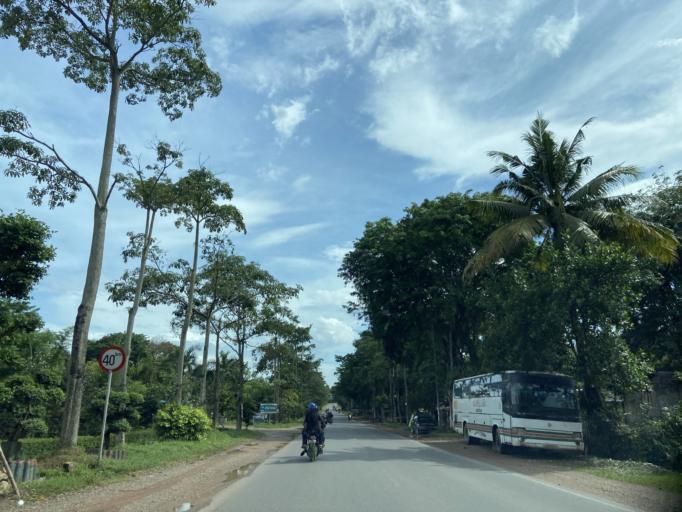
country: SG
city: Singapore
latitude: 1.0563
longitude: 103.9605
